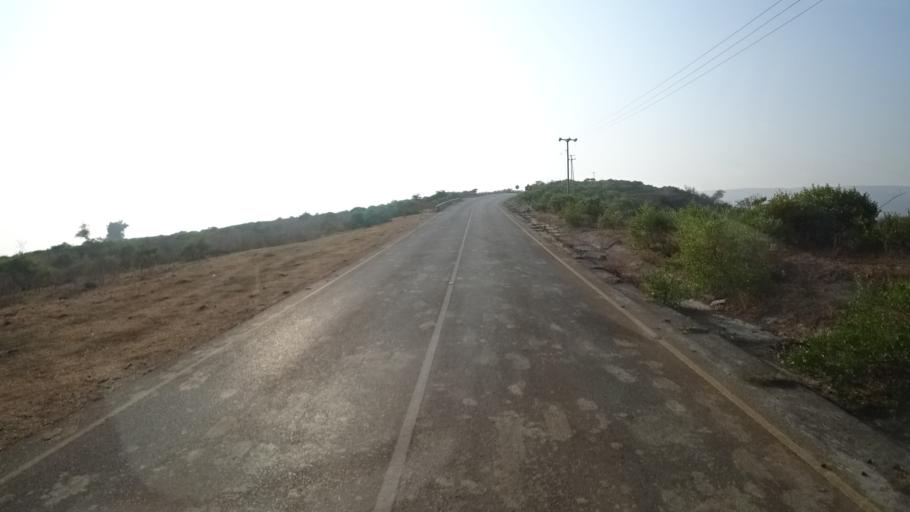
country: YE
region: Al Mahrah
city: Hawf
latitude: 16.7446
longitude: 53.3524
